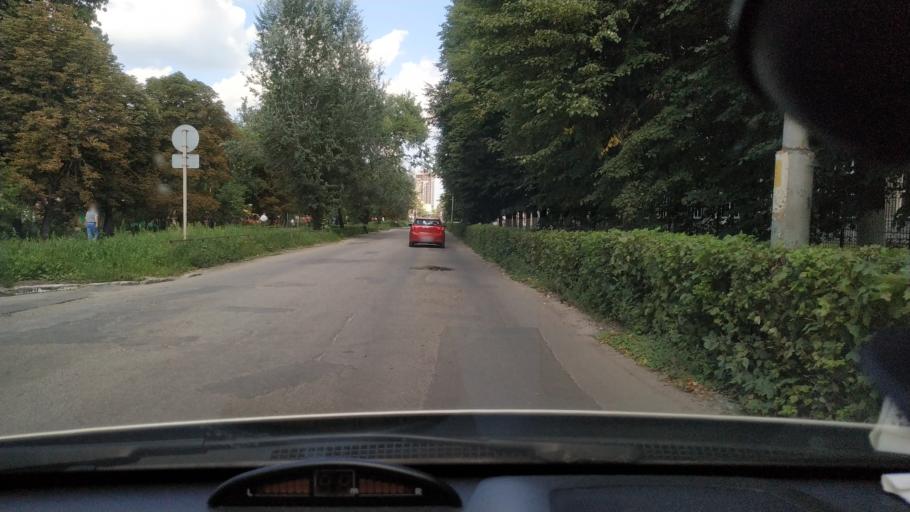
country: RU
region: Rjazan
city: Ryazan'
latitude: 54.6245
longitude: 39.7108
